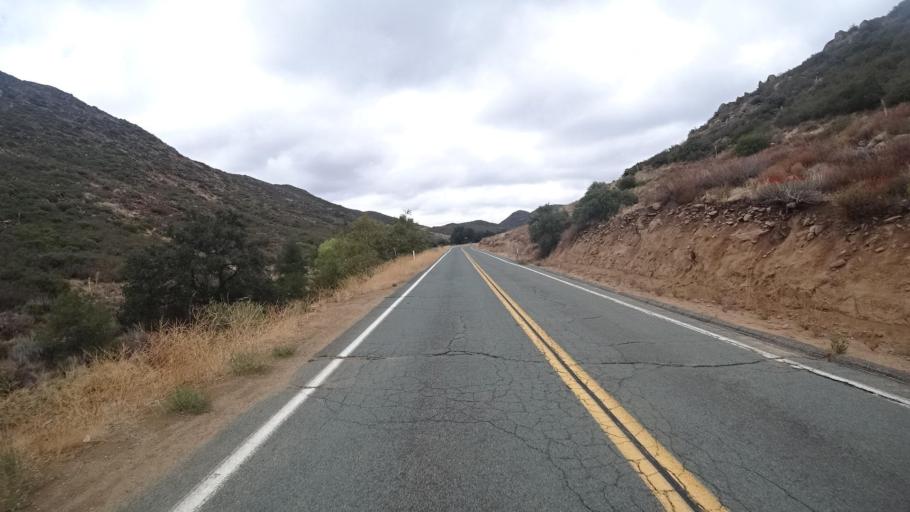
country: US
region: California
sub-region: San Diego County
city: Pine Valley
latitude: 32.7562
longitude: -116.4516
